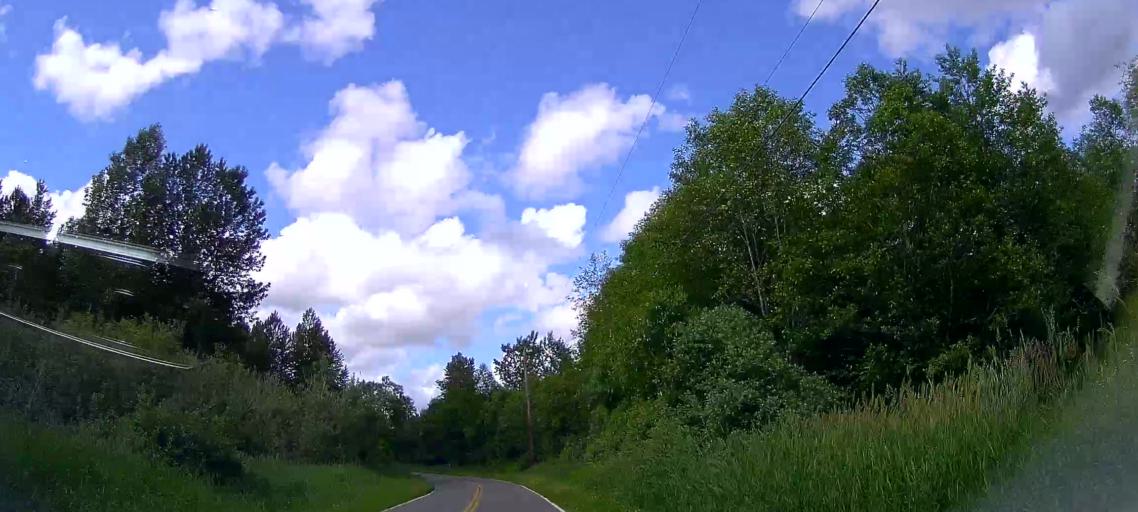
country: US
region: Washington
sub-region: Whatcom County
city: Sudden Valley
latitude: 48.6764
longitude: -122.1958
